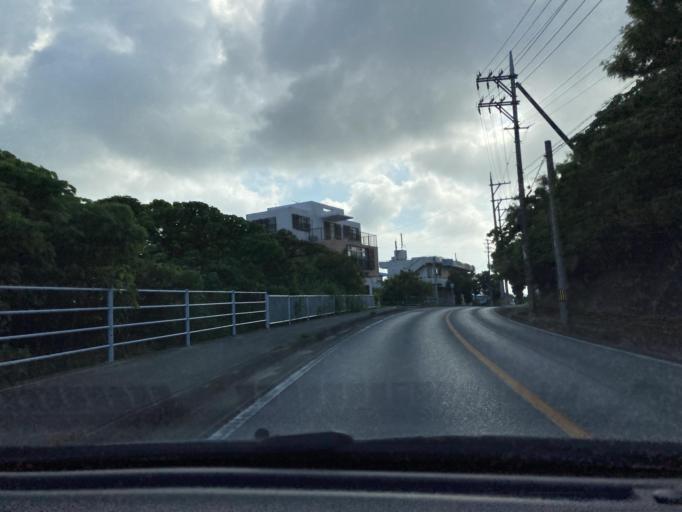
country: JP
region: Okinawa
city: Tomigusuku
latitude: 26.1726
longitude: 127.7329
